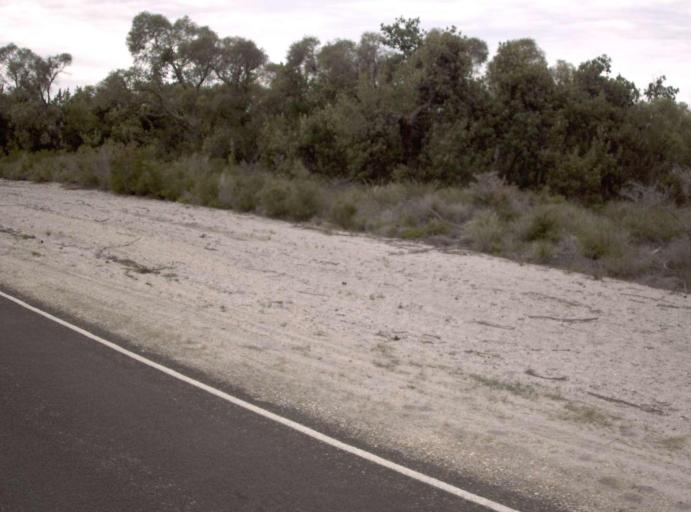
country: AU
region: Victoria
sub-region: Wellington
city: Sale
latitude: -38.1713
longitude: 147.3841
